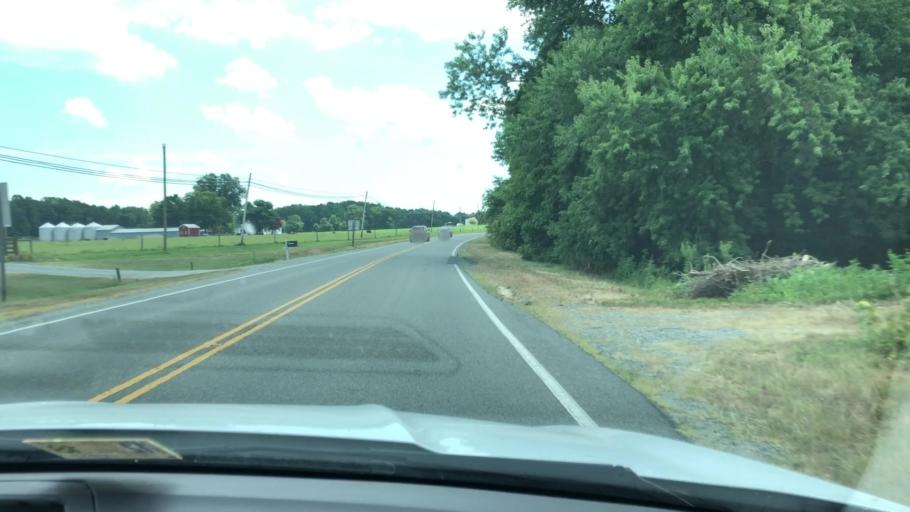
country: US
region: Virginia
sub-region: Lancaster County
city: Lancaster
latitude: 37.7950
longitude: -76.5208
